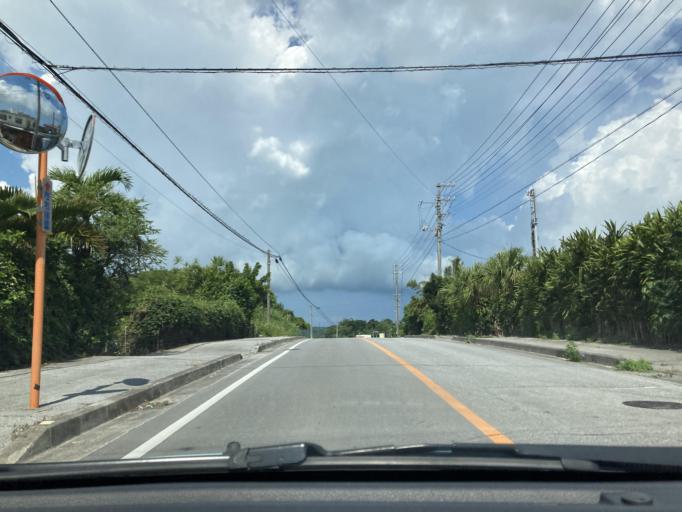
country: JP
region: Okinawa
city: Tomigusuku
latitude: 26.1583
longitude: 127.7786
